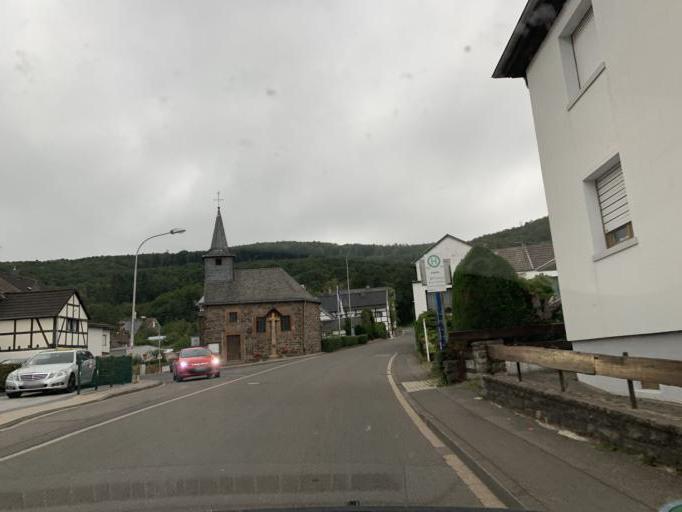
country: DE
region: North Rhine-Westphalia
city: Heimbach
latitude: 50.6390
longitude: 6.4588
